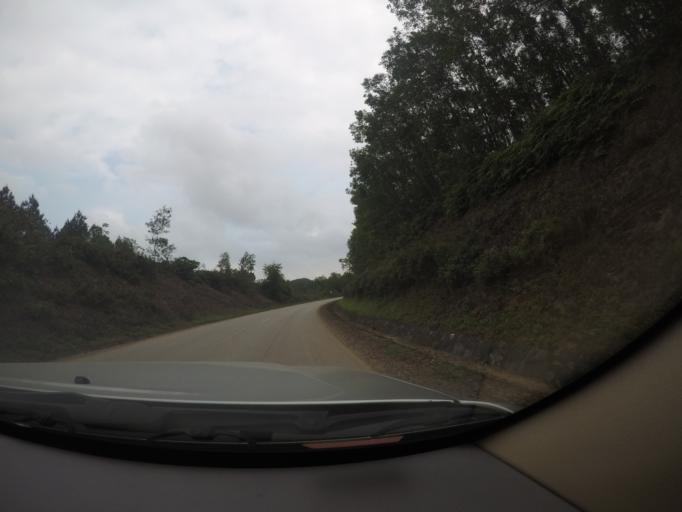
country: VN
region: Quang Binh
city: Kien Giang
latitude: 17.1353
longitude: 106.7747
